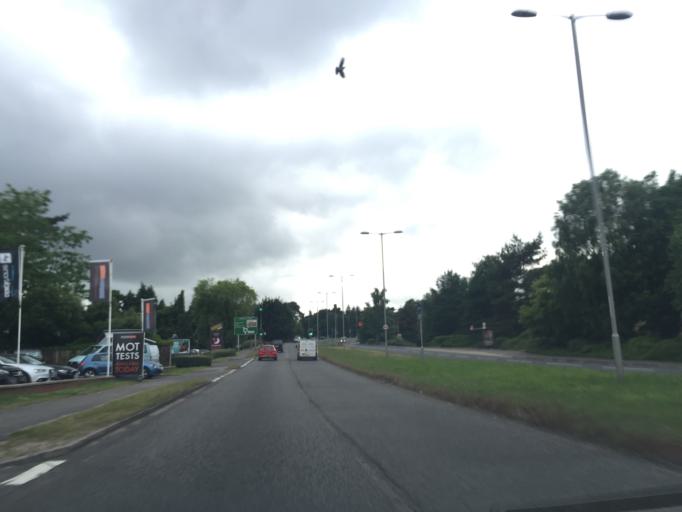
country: GB
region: England
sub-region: Dorset
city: Ferndown
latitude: 50.8117
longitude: -1.8737
